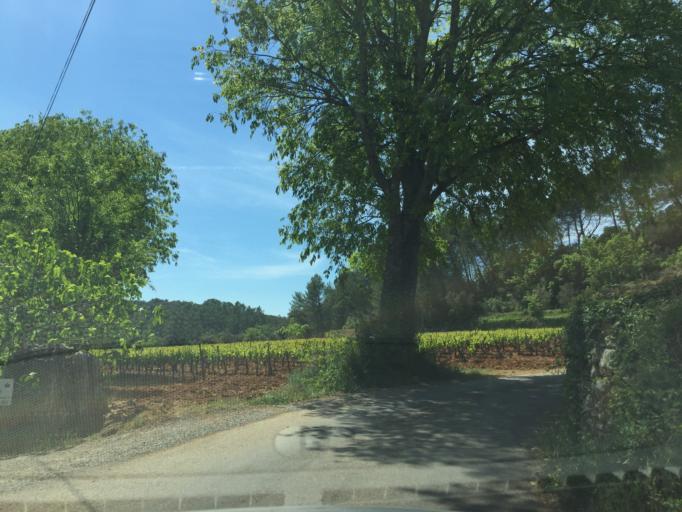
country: FR
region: Provence-Alpes-Cote d'Azur
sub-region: Departement du Var
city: Lorgues
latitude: 43.4793
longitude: 6.3680
